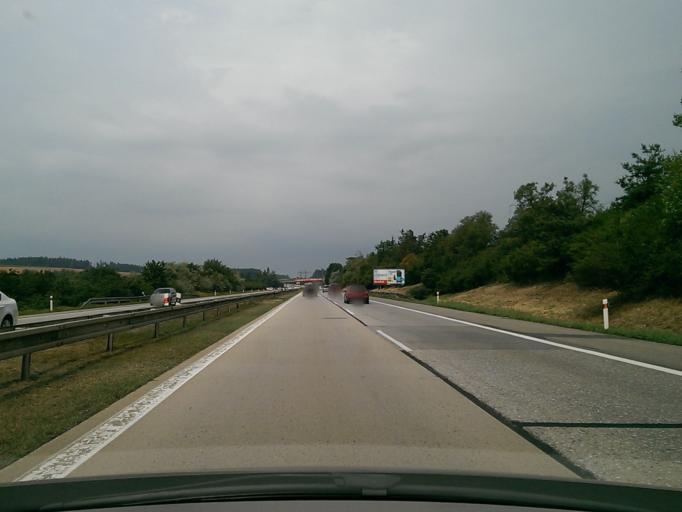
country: CZ
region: South Moravian
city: Ricany
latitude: 49.2496
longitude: 16.3564
